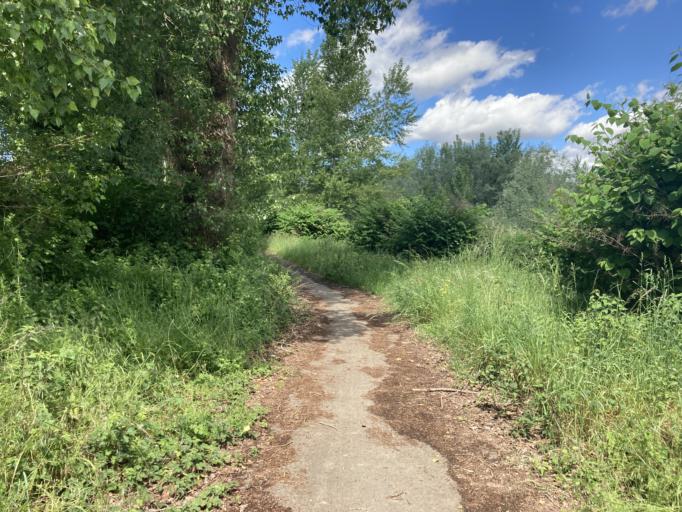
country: FR
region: Aquitaine
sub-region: Departement des Pyrenees-Atlantiques
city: Arbus
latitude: 43.3395
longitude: -0.4995
